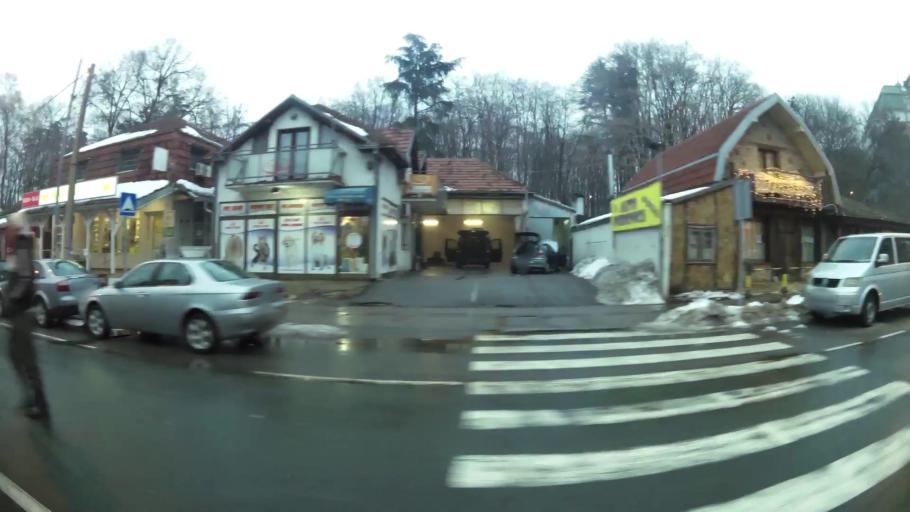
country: RS
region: Central Serbia
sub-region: Belgrade
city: Vozdovac
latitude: 44.7715
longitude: 20.4934
